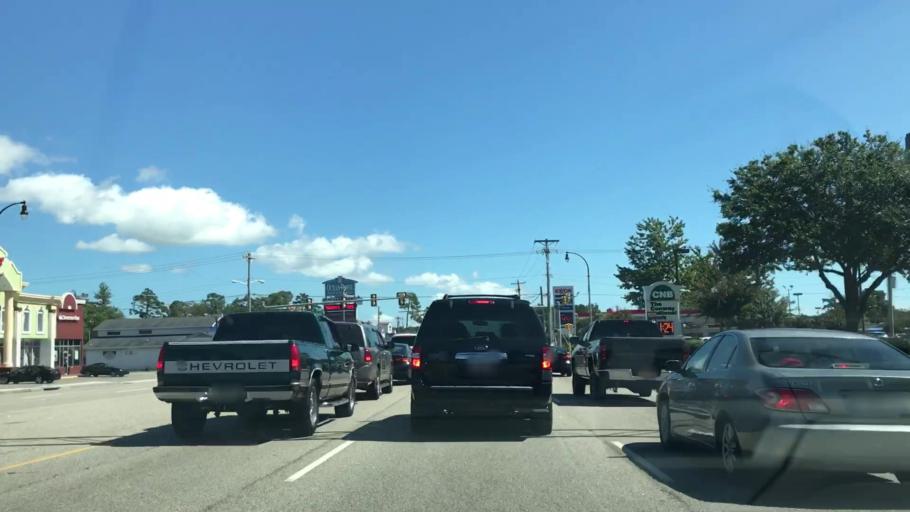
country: US
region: South Carolina
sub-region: Horry County
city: North Myrtle Beach
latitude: 33.8292
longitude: -78.6787
